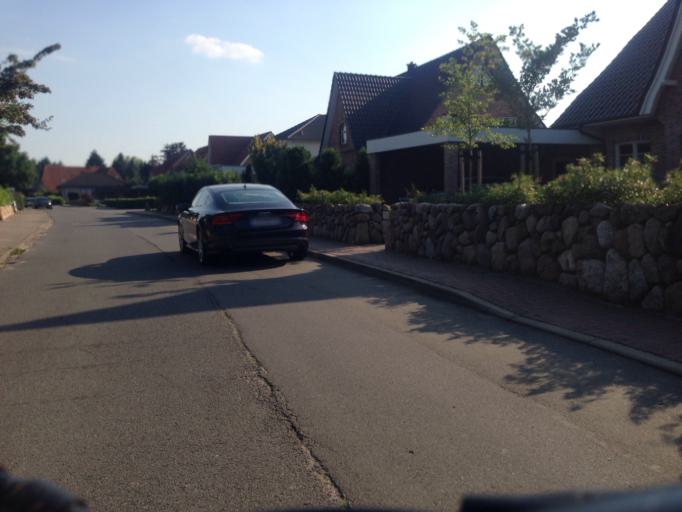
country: DE
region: Lower Saxony
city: Adendorf
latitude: 53.2890
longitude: 10.4402
